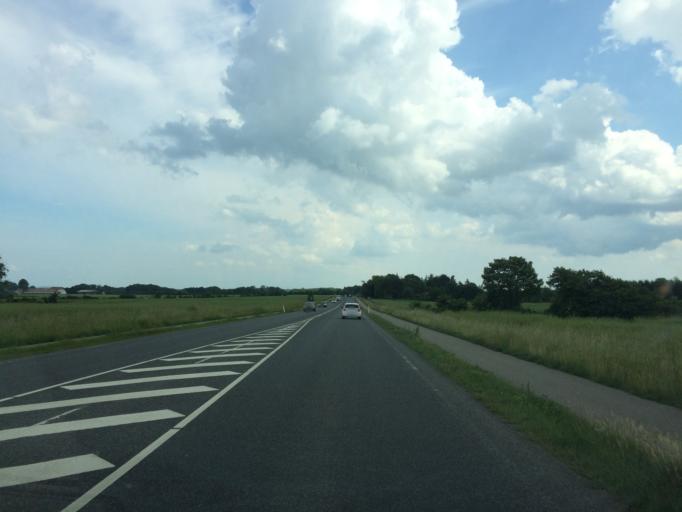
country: DK
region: South Denmark
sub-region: Vejle Kommune
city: Borkop
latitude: 55.6031
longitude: 9.6264
